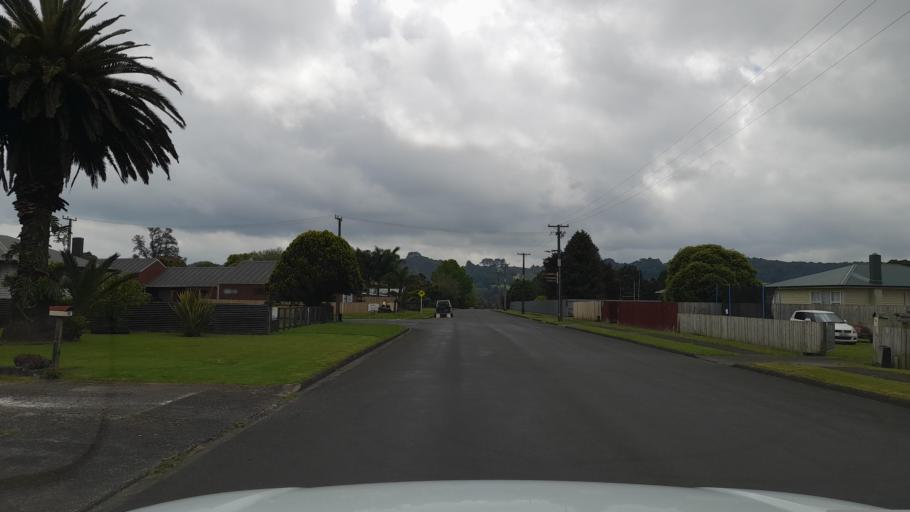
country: NZ
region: Northland
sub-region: Far North District
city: Waimate North
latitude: -35.4086
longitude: 173.7914
